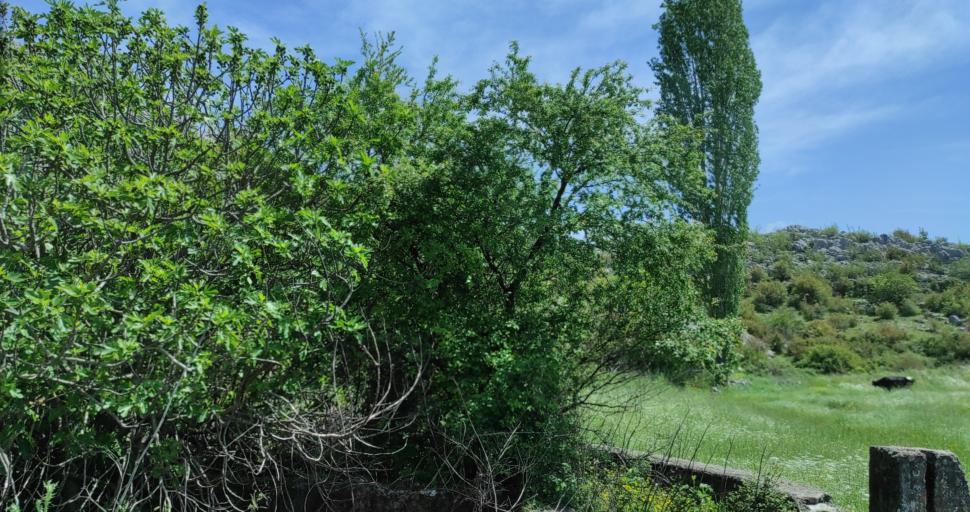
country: AL
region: Shkoder
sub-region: Rrethi i Malesia e Madhe
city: Gruemire
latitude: 42.1455
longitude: 19.5448
